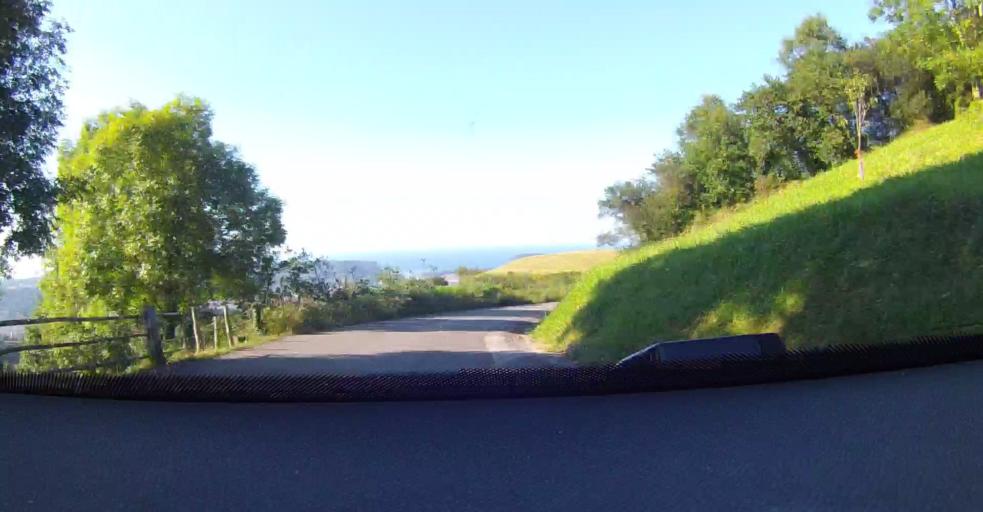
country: ES
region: Asturias
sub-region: Province of Asturias
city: Villaviciosa
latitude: 43.4877
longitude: -5.3918
